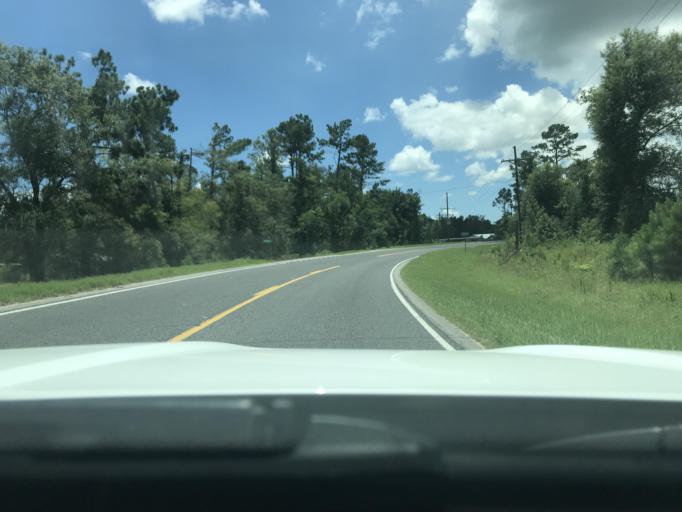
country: US
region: Louisiana
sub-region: Calcasieu Parish
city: Moss Bluff
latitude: 30.2791
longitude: -93.1681
